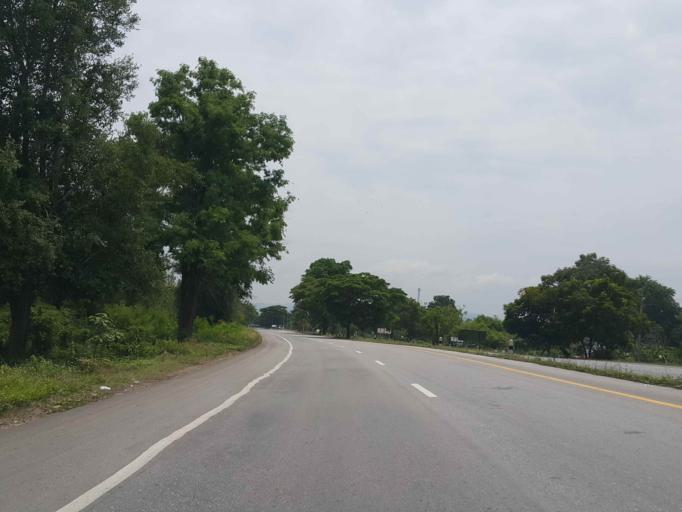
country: TH
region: Lampang
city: Sop Prap
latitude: 17.9129
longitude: 99.3421
